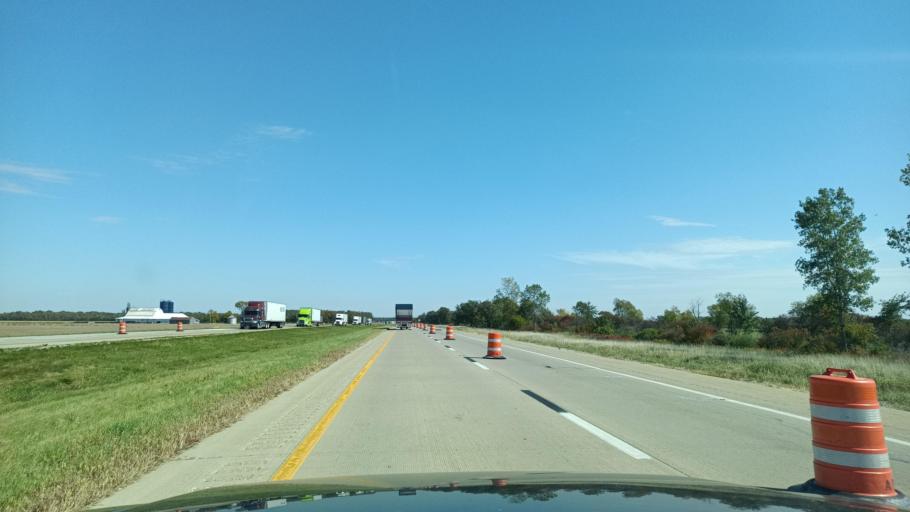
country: US
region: Ohio
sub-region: Defiance County
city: Defiance
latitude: 41.2548
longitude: -84.4632
